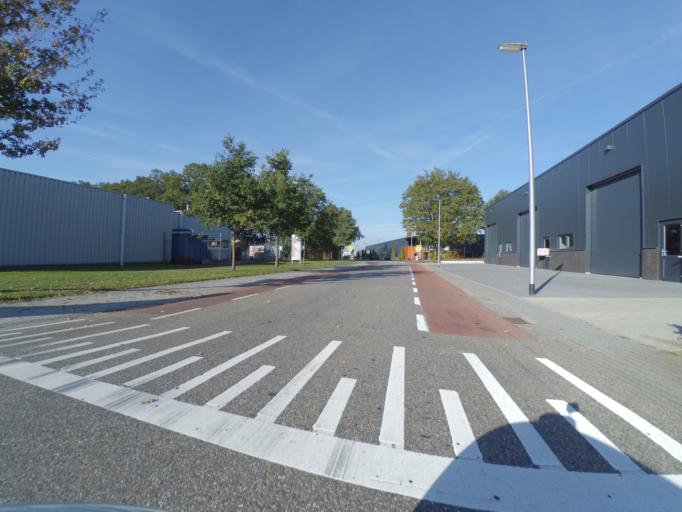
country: NL
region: Gelderland
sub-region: Berkelland
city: Eibergen
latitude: 52.0878
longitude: 6.6407
